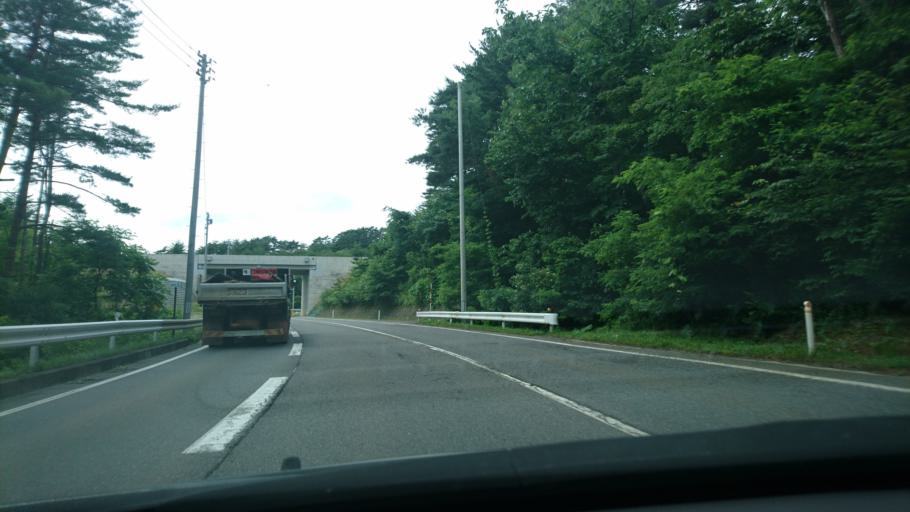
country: JP
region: Aomori
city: Hachinohe
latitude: 40.2301
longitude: 141.7822
